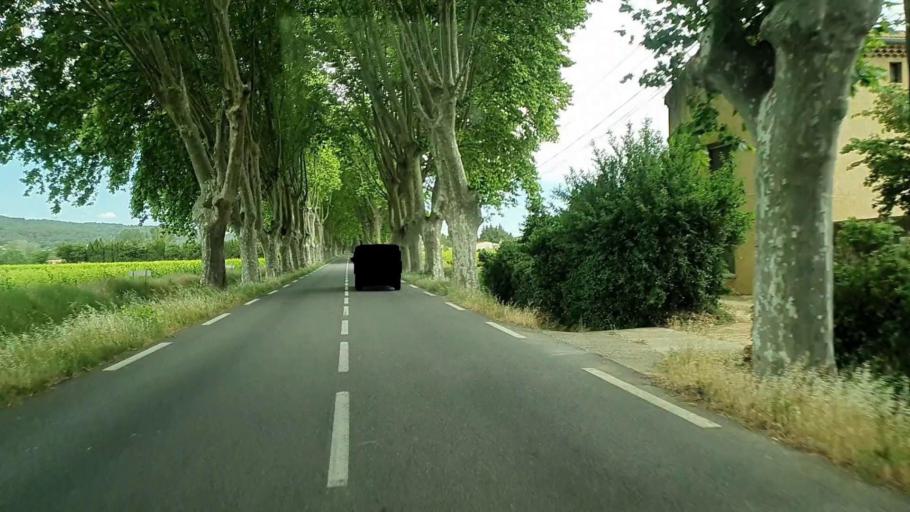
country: FR
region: Languedoc-Roussillon
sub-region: Departement du Gard
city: Tresques
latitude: 44.1226
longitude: 4.6149
